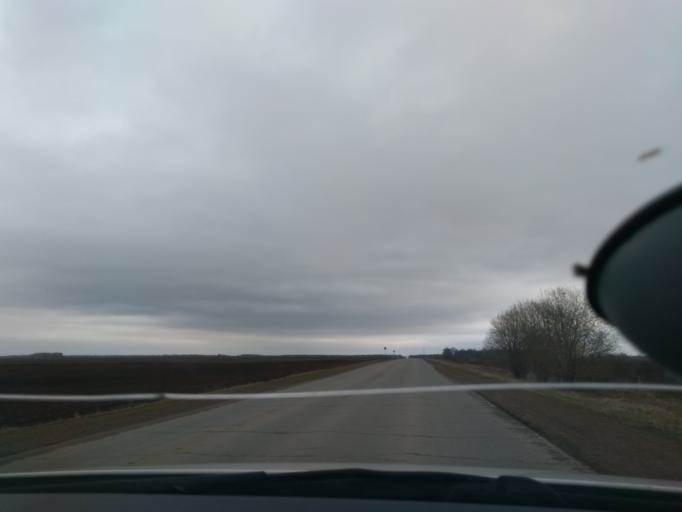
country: RU
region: Perm
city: Kungur
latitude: 57.3767
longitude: 56.8439
